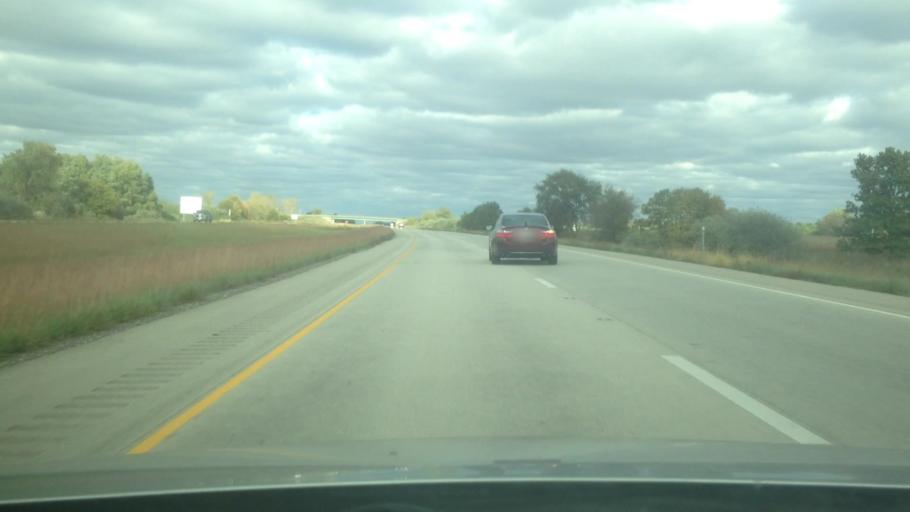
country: US
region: Illinois
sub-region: Macon County
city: Forsyth
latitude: 39.9142
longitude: -88.8673
